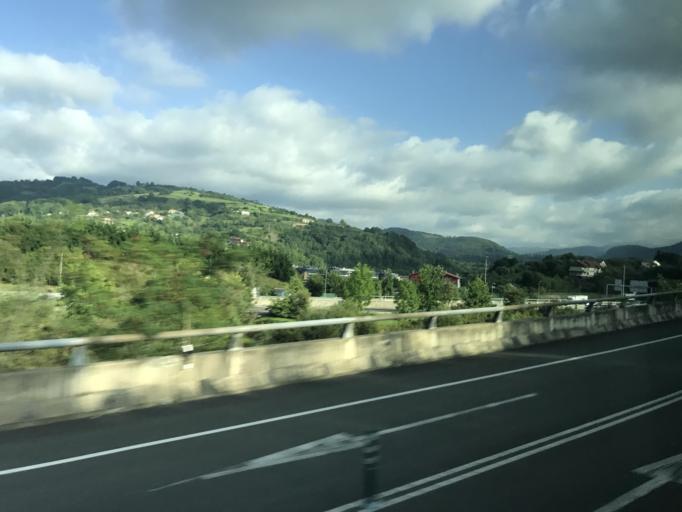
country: ES
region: Basque Country
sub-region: Provincia de Guipuzcoa
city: Astigarraga
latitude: 43.2836
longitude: -1.9599
